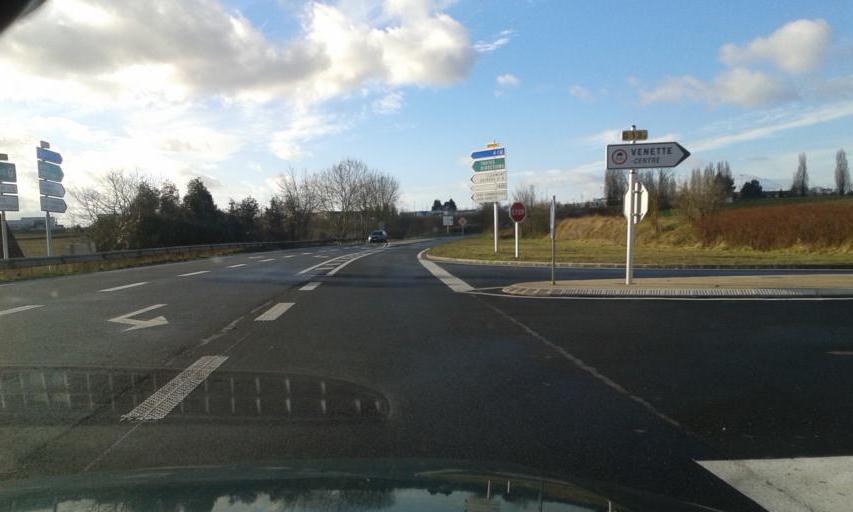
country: FR
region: Picardie
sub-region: Departement de l'Oise
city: Venette
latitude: 49.4082
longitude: 2.7926
